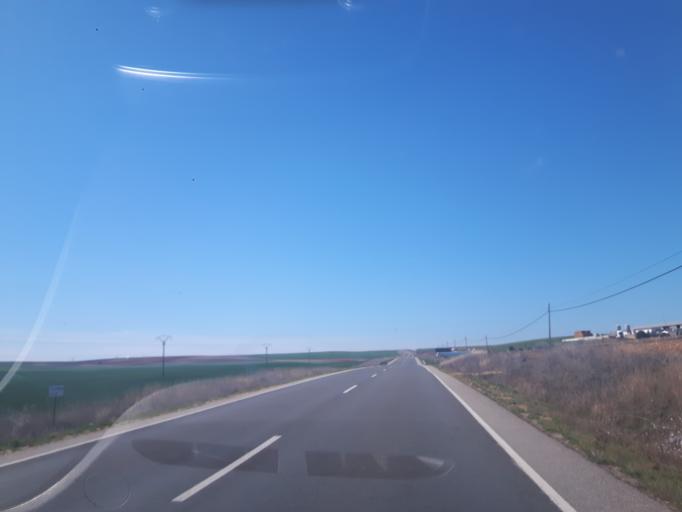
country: ES
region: Castille and Leon
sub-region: Provincia de Salamanca
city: Aldeaseca de Alba
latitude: 40.8397
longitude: -5.4711
